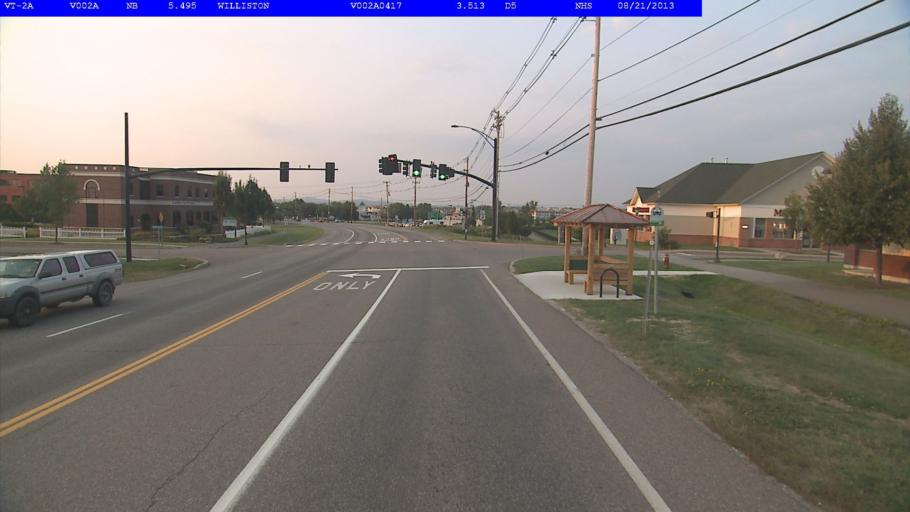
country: US
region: Vermont
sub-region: Chittenden County
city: Williston
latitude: 44.4465
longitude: -73.1111
